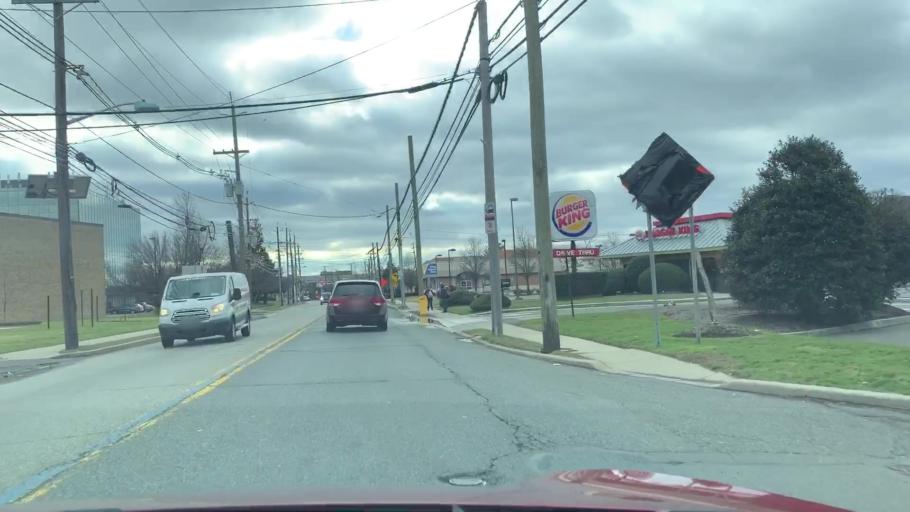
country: US
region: New Jersey
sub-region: Bergen County
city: Moonachie
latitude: 40.8355
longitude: -74.0519
